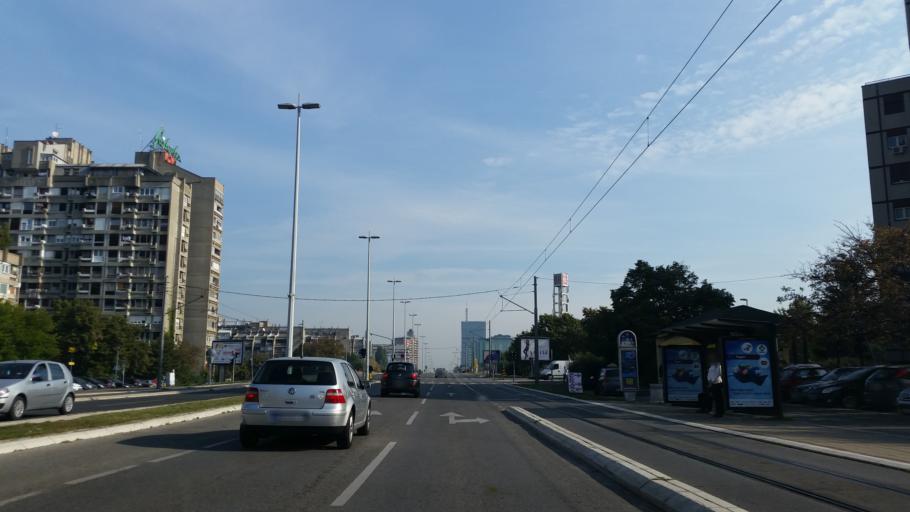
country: RS
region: Central Serbia
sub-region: Belgrade
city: Novi Beograd
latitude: 44.8066
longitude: 20.4274
